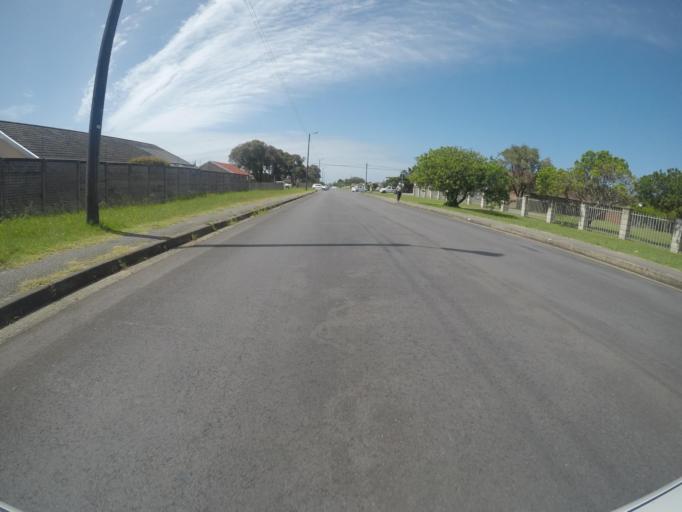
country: ZA
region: Eastern Cape
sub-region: Buffalo City Metropolitan Municipality
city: East London
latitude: -32.9498
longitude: 27.9970
